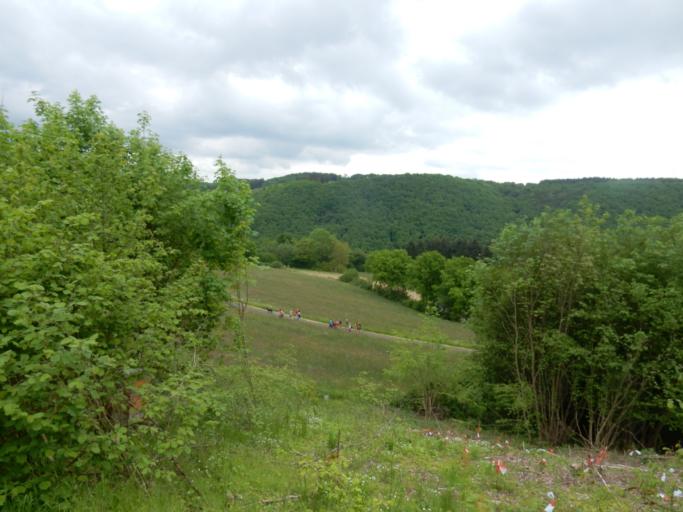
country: LU
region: Diekirch
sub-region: Canton de Diekirch
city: Erpeldange
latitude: 49.8861
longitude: 6.1045
